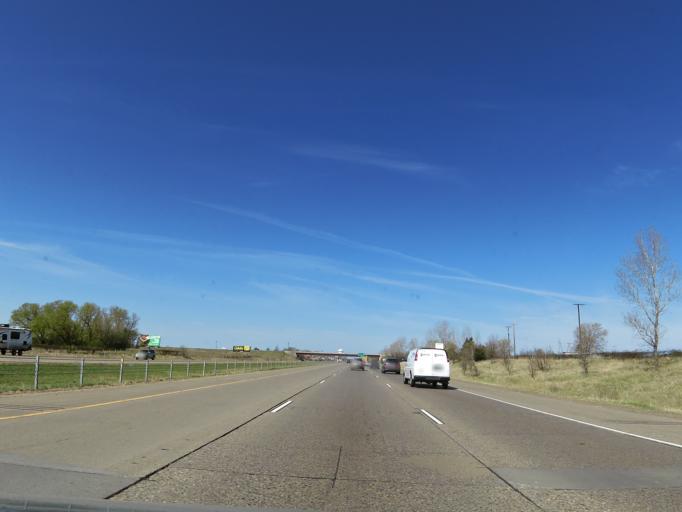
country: US
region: Minnesota
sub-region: Washington County
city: Lake Elmo
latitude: 44.9488
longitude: -92.8771
